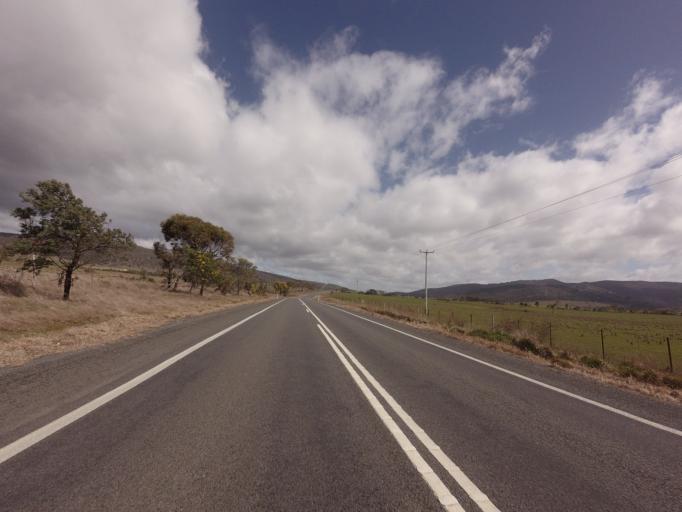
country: AU
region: Tasmania
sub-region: Northern Midlands
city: Evandale
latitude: -41.8114
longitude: 147.6434
